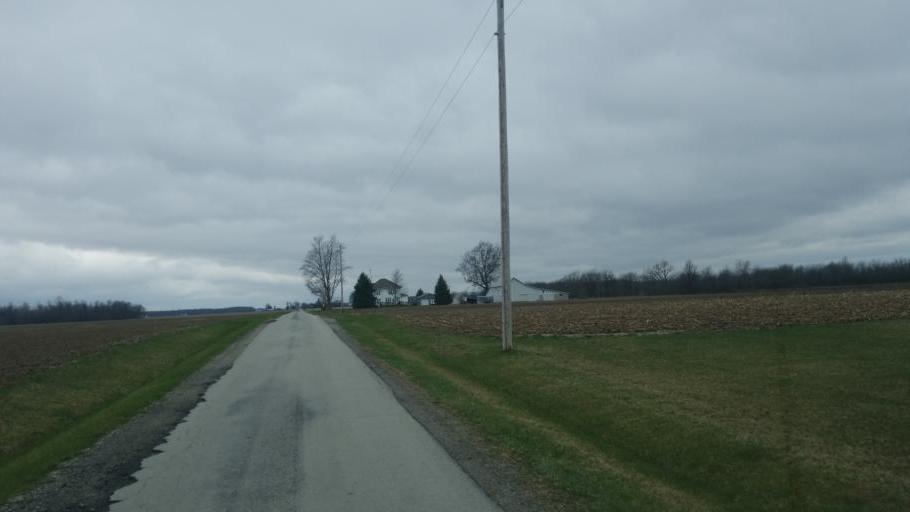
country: US
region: Ohio
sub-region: Hardin County
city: Forest
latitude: 40.7234
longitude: -83.4817
